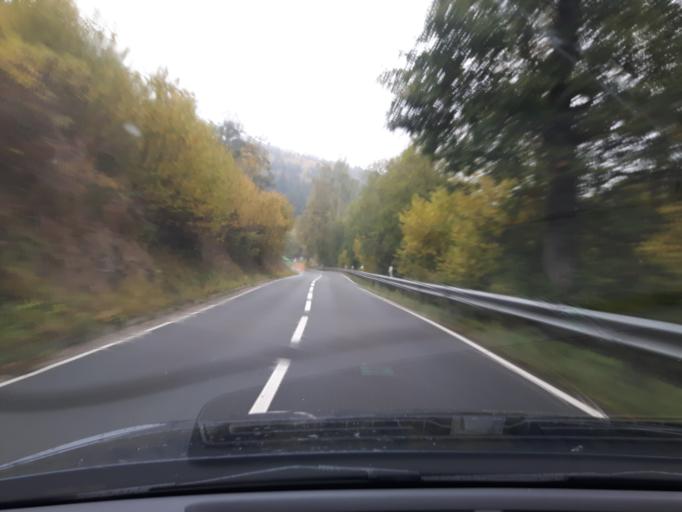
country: DE
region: North Rhine-Westphalia
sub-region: Regierungsbezirk Arnsberg
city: Bad Laasphe
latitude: 50.9516
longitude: 8.3975
